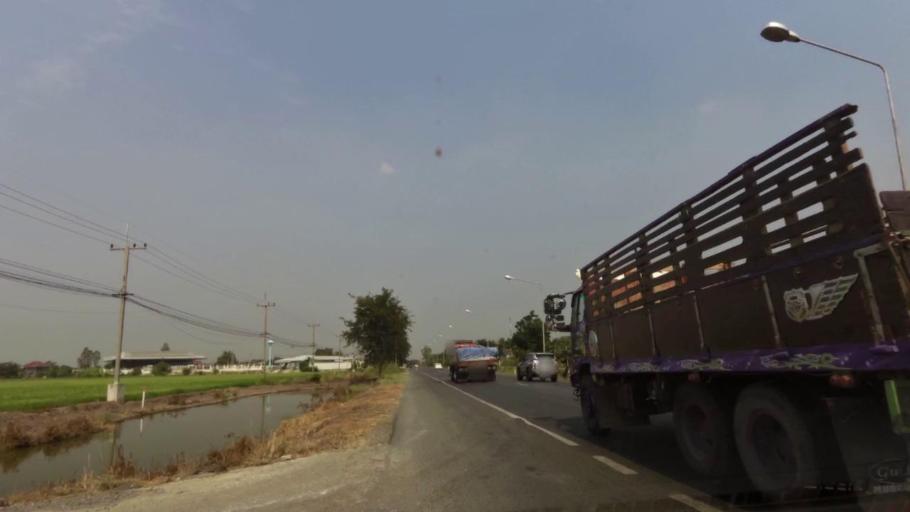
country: TH
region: Phra Nakhon Si Ayutthaya
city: Phra Nakhon Si Ayutthaya
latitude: 14.3114
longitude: 100.5254
